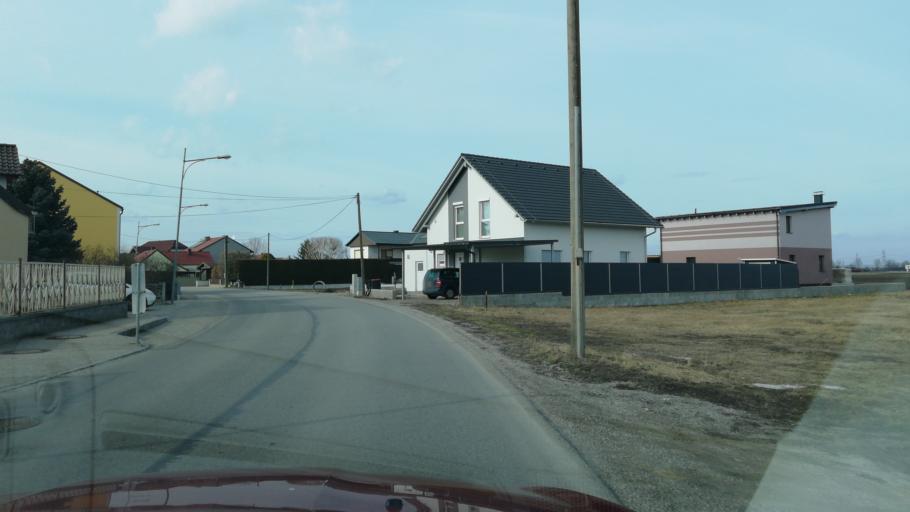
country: AT
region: Lower Austria
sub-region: Politischer Bezirk Tulln
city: Atzenbrugg
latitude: 48.3063
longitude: 15.9026
